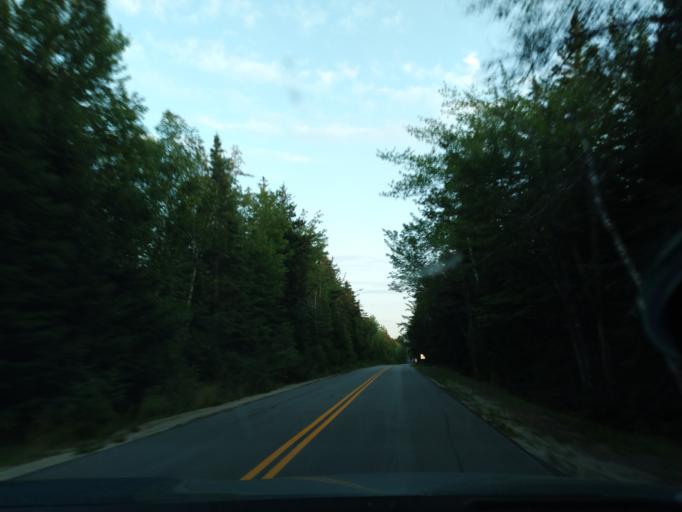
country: US
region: Maine
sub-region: Hancock County
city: Gouldsboro
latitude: 44.3866
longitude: -68.0700
